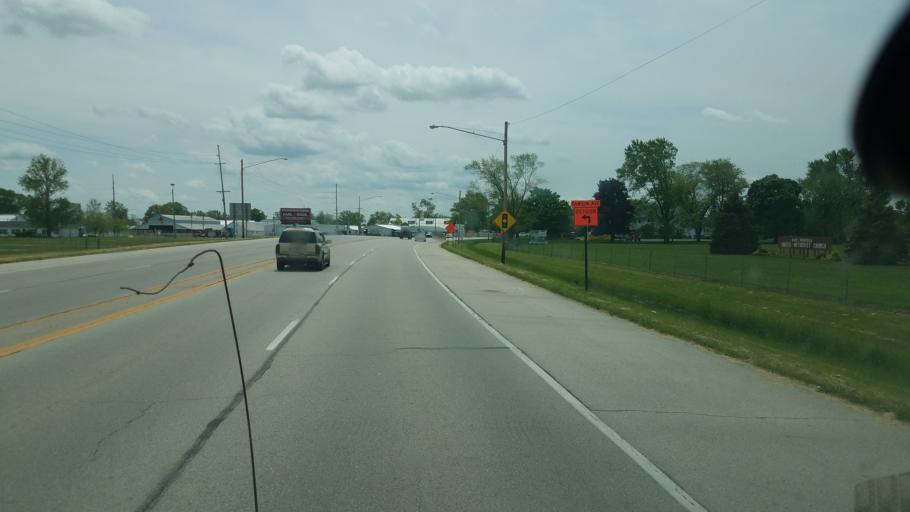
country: US
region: Ohio
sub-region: Sandusky County
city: Fremont
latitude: 41.3637
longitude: -83.1172
